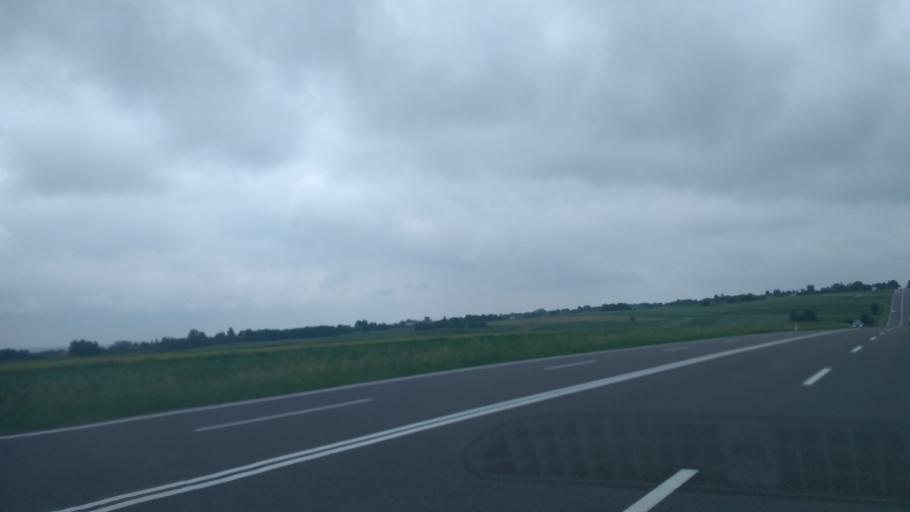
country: PL
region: Subcarpathian Voivodeship
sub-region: Powiat lancucki
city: Rogozno
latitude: 50.0697
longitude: 22.3554
